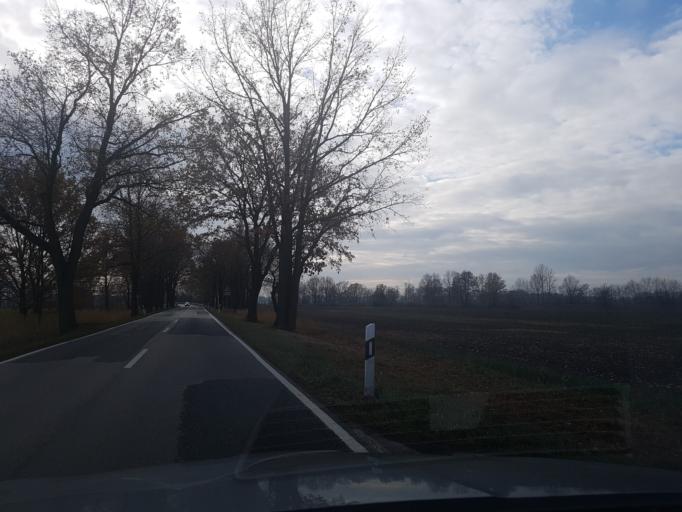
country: DE
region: Brandenburg
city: Plessa
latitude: 51.4484
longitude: 13.6210
